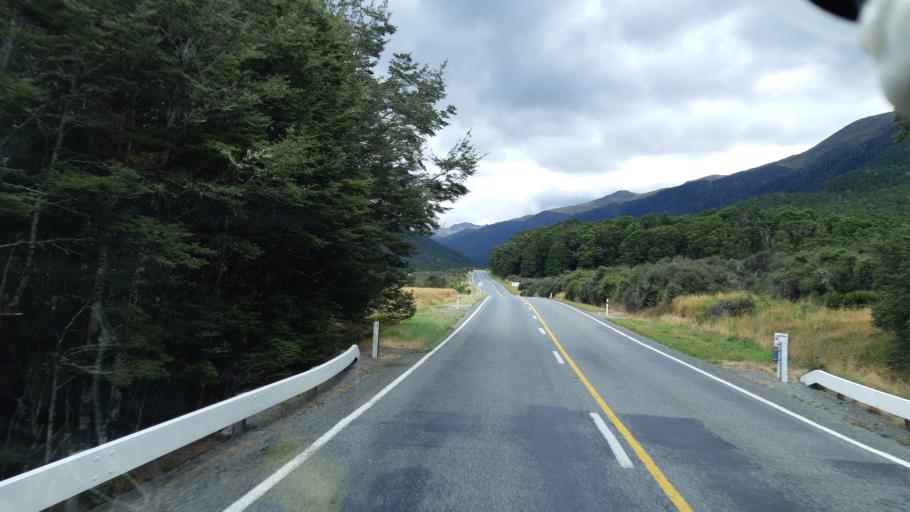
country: NZ
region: Canterbury
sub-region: Hurunui District
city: Amberley
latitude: -42.4848
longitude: 172.3897
